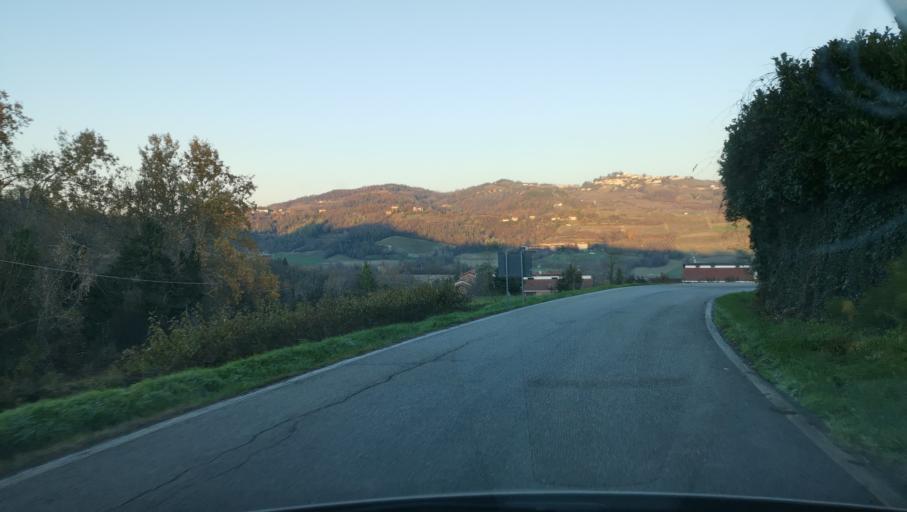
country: IT
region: Piedmont
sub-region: Provincia di Asti
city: Moncucco Torinese
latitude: 45.0626
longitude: 7.9356
